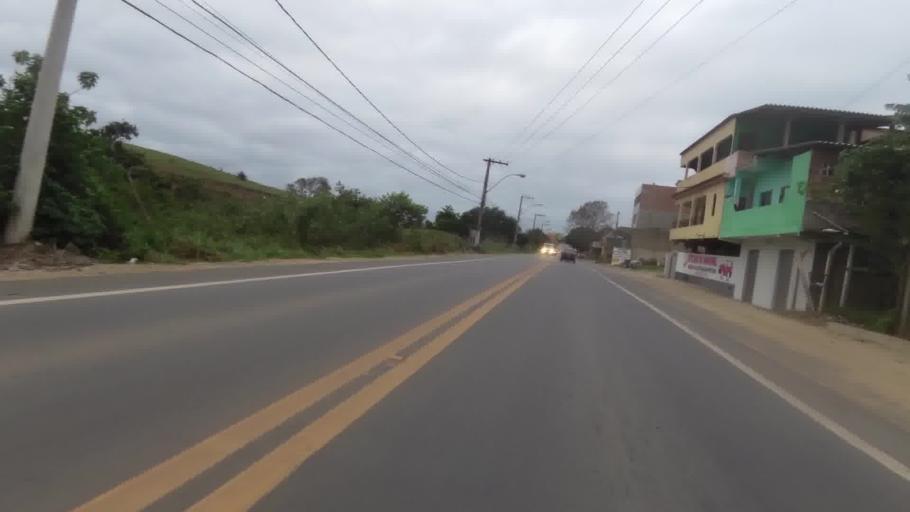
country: BR
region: Espirito Santo
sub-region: Piuma
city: Piuma
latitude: -20.8345
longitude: -40.7142
